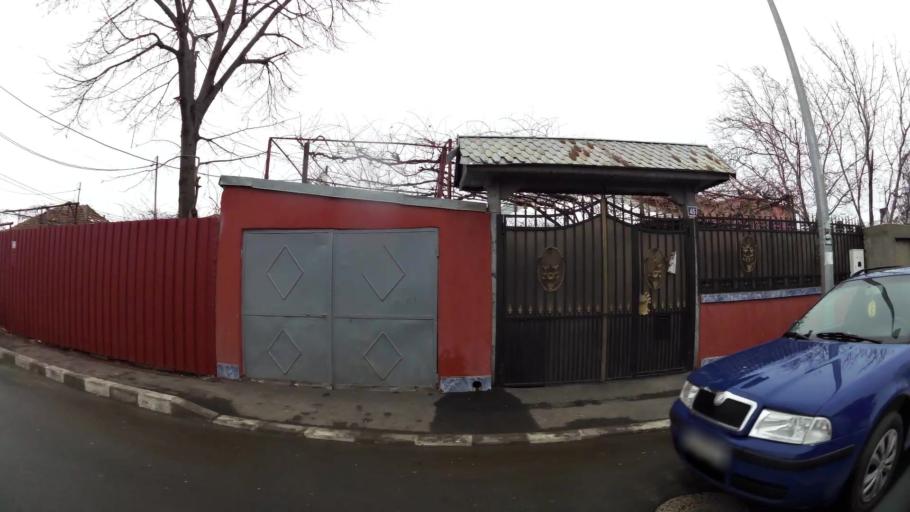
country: RO
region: Ilfov
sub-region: Comuna Pantelimon
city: Pantelimon
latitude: 44.4571
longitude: 26.2027
